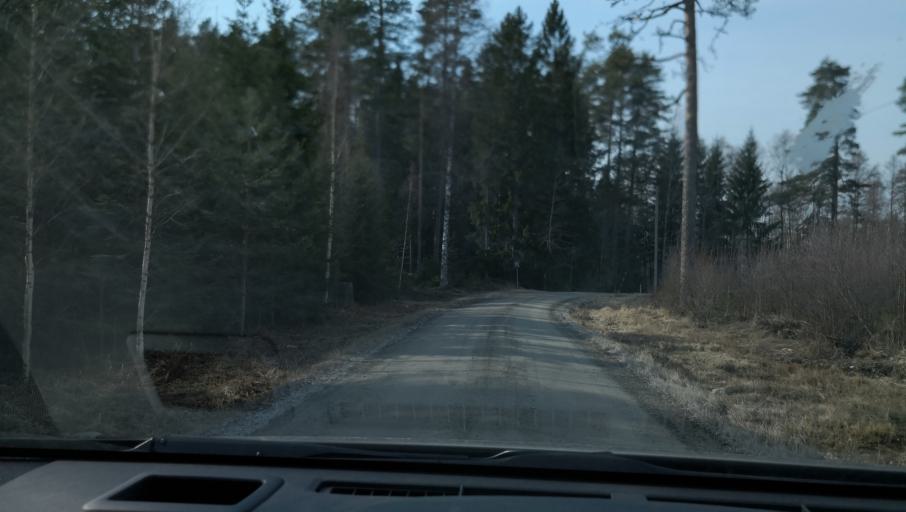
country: SE
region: OErebro
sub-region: Lindesbergs Kommun
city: Frovi
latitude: 59.3641
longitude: 15.4307
